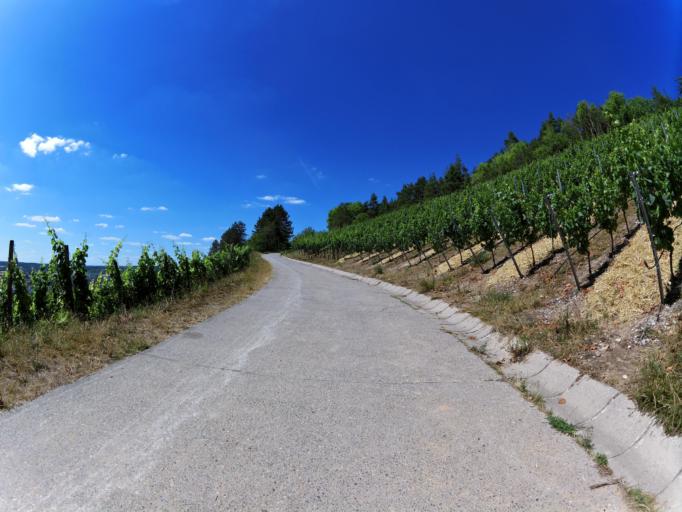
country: DE
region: Bavaria
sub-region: Regierungsbezirk Unterfranken
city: Thungersheim
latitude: 49.8908
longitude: 9.8458
